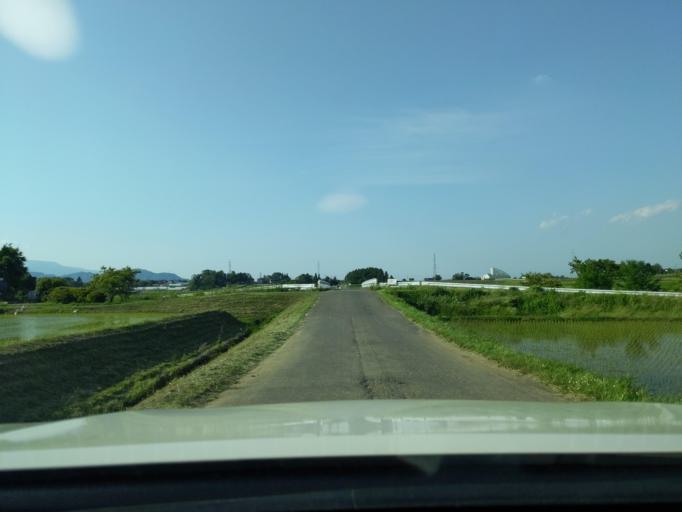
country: JP
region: Fukushima
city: Koriyama
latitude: 37.4470
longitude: 140.3648
